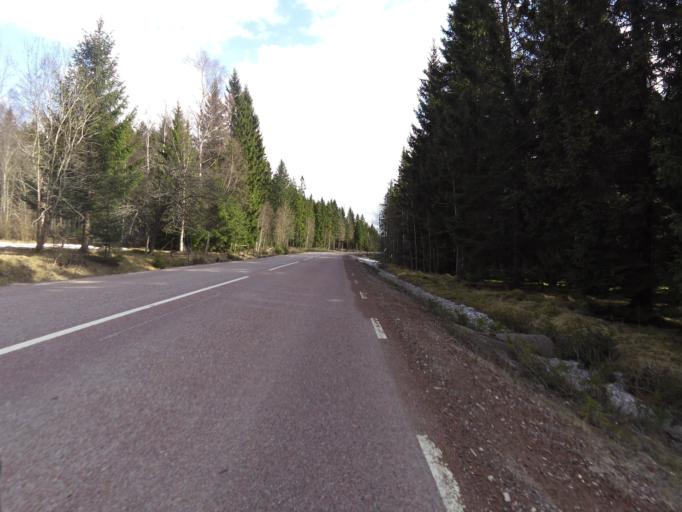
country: SE
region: Dalarna
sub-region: Avesta Kommun
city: Horndal
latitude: 60.3073
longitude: 16.2444
